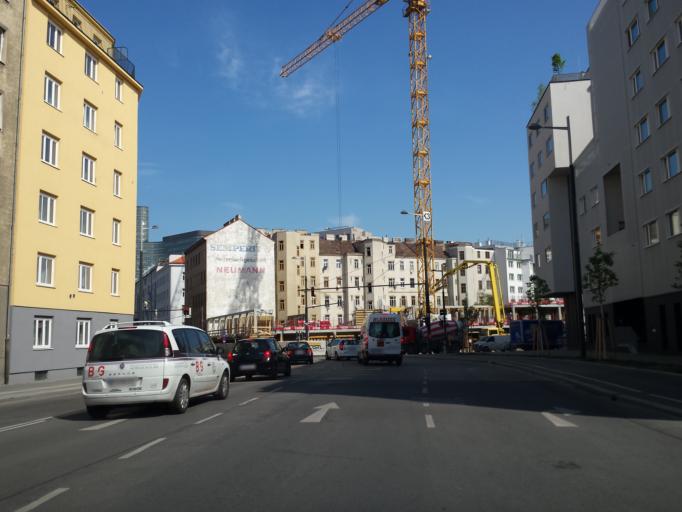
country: AT
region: Vienna
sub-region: Wien Stadt
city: Vienna
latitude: 48.1808
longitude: 16.3795
